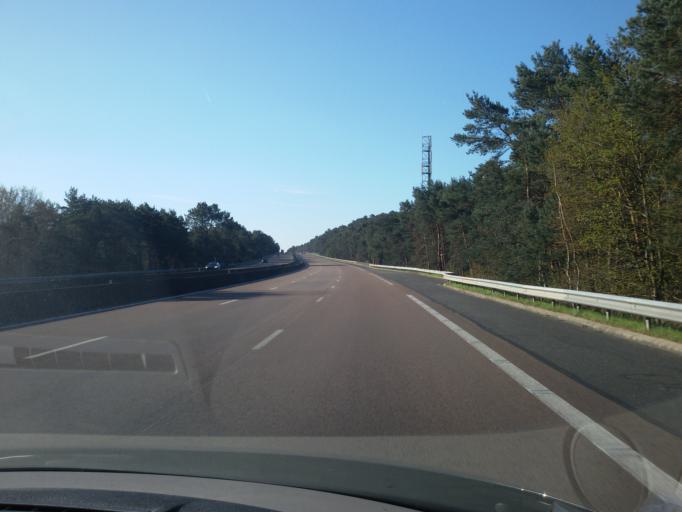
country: FR
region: Ile-de-France
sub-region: Departement de Seine-et-Marne
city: Arbonne-la-Foret
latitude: 48.3912
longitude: 2.5544
